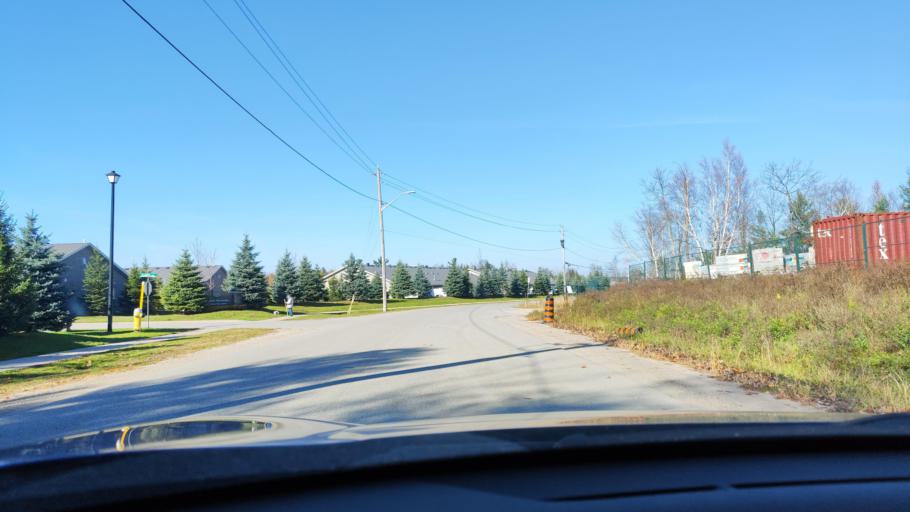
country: CA
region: Ontario
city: Wasaga Beach
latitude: 44.5277
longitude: -79.9970
